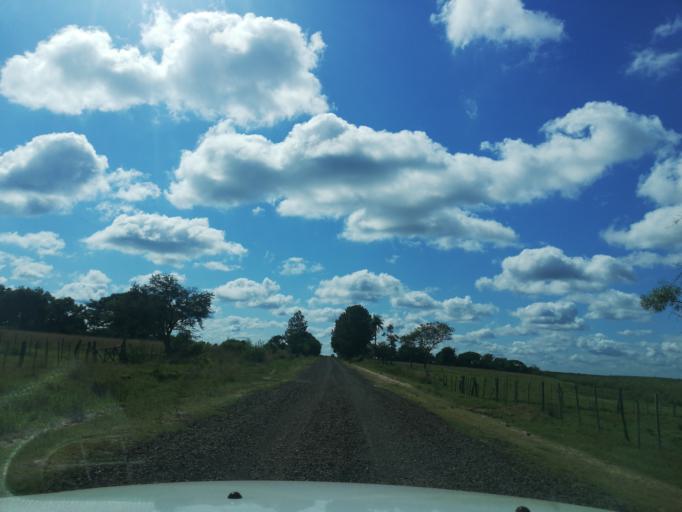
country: AR
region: Corrientes
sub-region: Departamento de San Miguel
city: San Miguel
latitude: -27.9832
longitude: -57.5776
